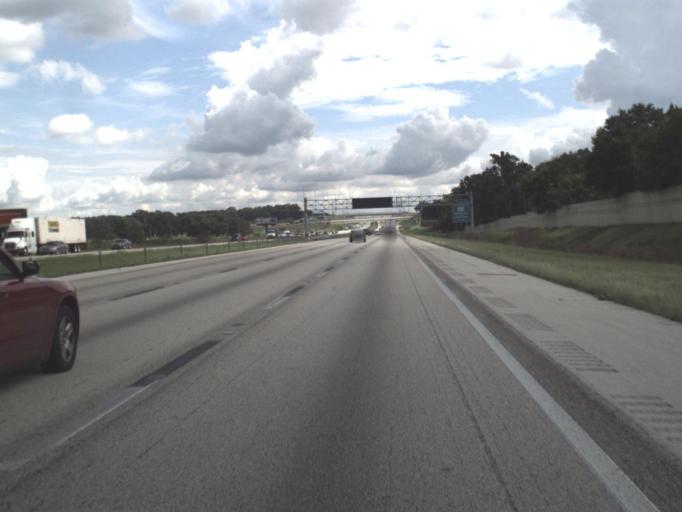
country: US
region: Florida
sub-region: Polk County
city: Winston
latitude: 28.0629
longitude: -82.0000
